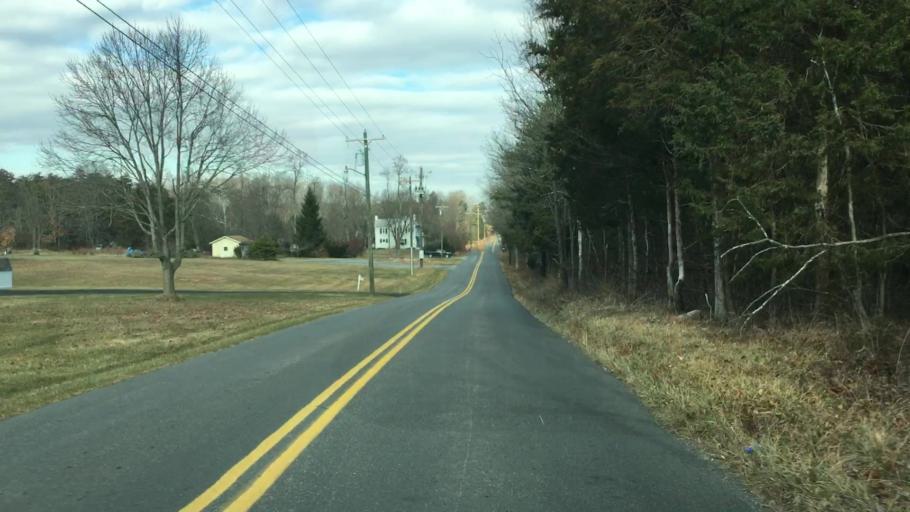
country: US
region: Virginia
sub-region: Warren County
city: Front Royal
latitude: 38.9500
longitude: -78.2561
